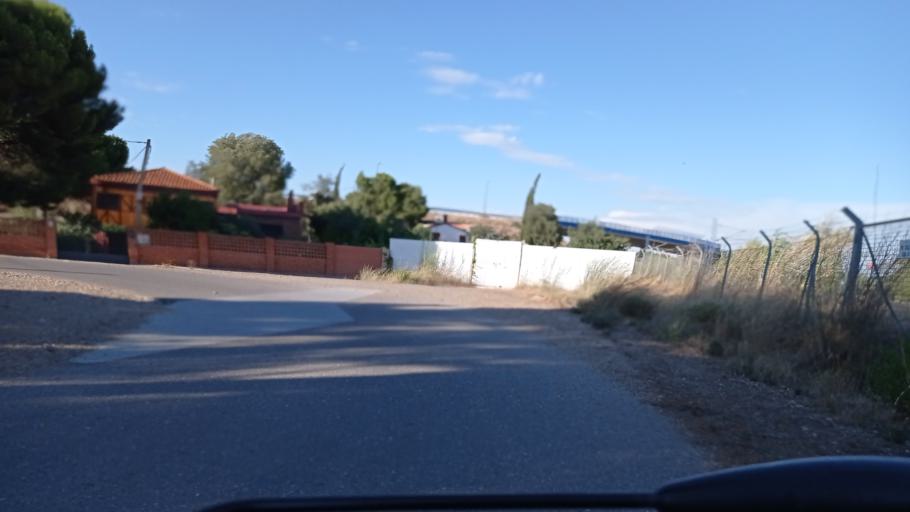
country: ES
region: Aragon
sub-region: Provincia de Zaragoza
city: Oliver-Valdefierro, Oliver, Valdefierro
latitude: 41.6601
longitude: -0.9504
